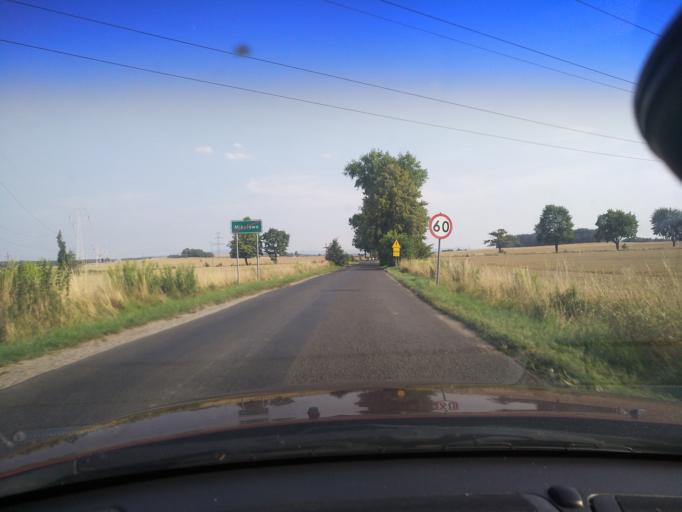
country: PL
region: Lower Silesian Voivodeship
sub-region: Powiat zgorzelecki
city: Sulikow
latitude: 51.0807
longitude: 15.1023
